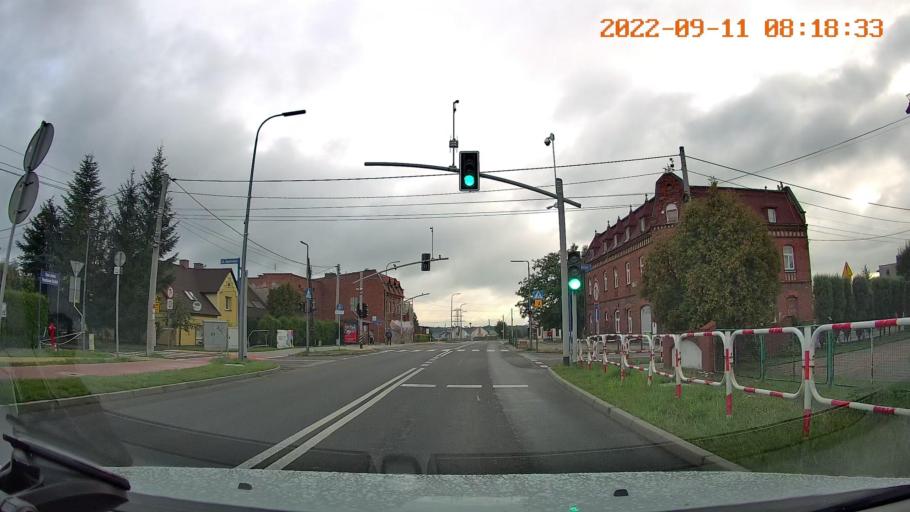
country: PL
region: Silesian Voivodeship
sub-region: Tychy
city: Tychy
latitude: 50.1461
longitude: 18.9991
